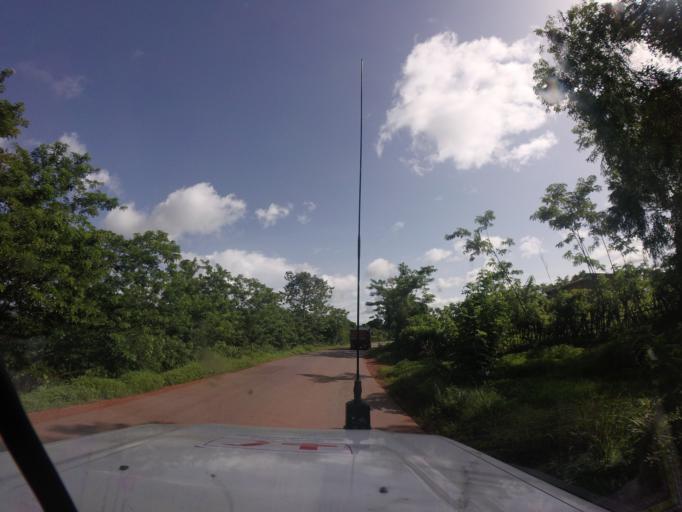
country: GN
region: Mamou
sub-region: Mamou Prefecture
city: Mamou
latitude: 10.2826
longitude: -12.3831
